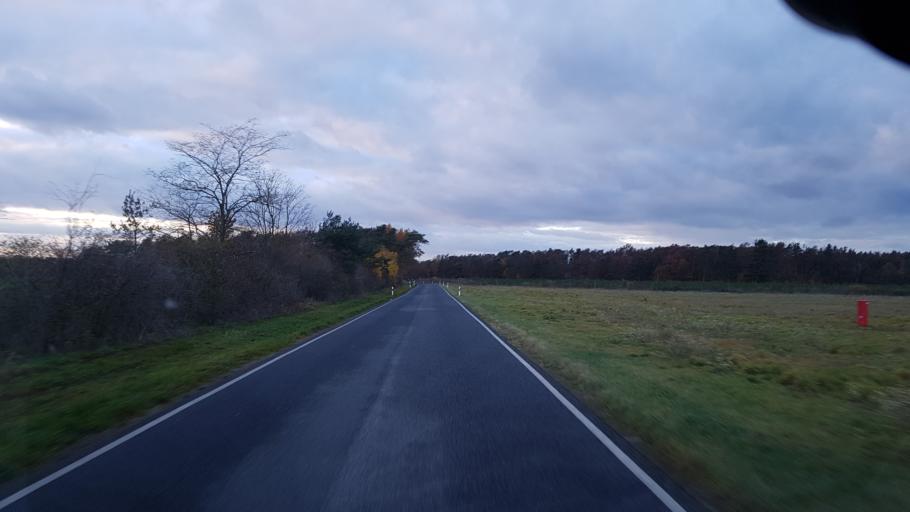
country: DE
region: Brandenburg
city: Tettau
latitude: 51.4234
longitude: 13.7464
